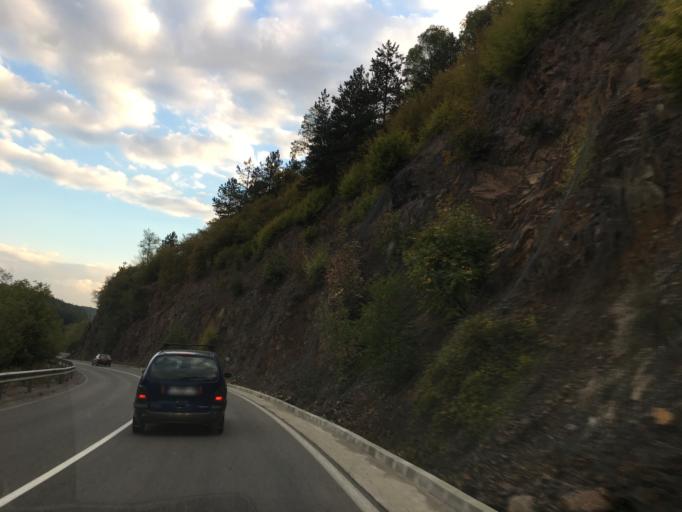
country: BG
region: Sofiya
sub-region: Obshtina Svoge
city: Svoge
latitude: 42.8744
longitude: 23.3755
